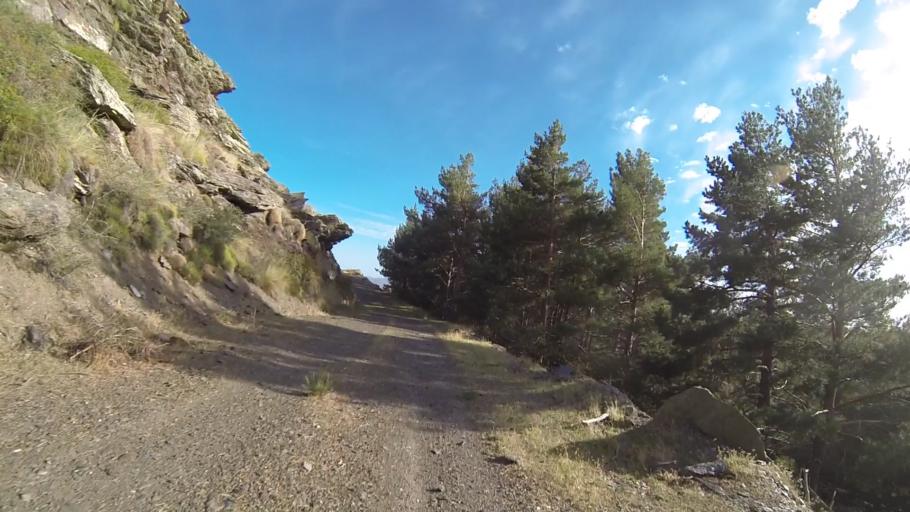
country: ES
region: Andalusia
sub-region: Provincia de Almeria
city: Paterna del Rio
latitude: 37.0732
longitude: -2.8948
